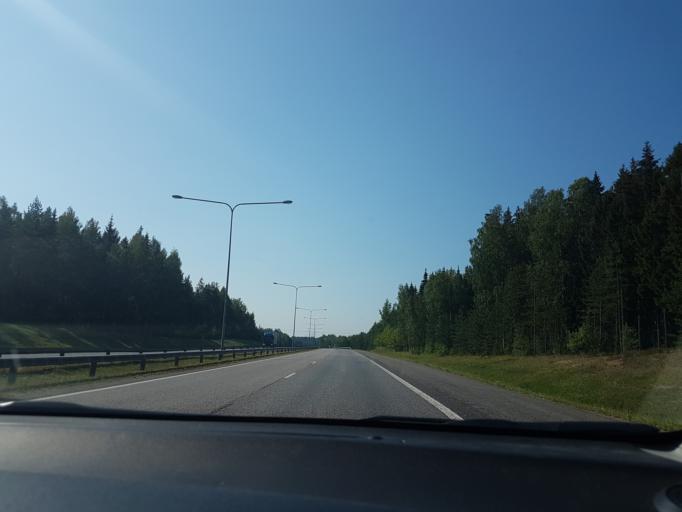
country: FI
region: Uusimaa
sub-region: Helsinki
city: Tuusula
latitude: 60.3531
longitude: 25.0001
